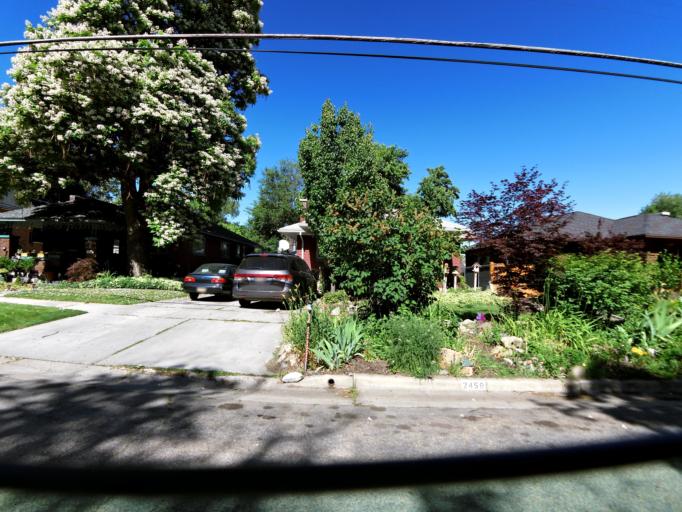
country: US
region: Utah
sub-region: Weber County
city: Ogden
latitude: 41.2211
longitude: -111.9455
